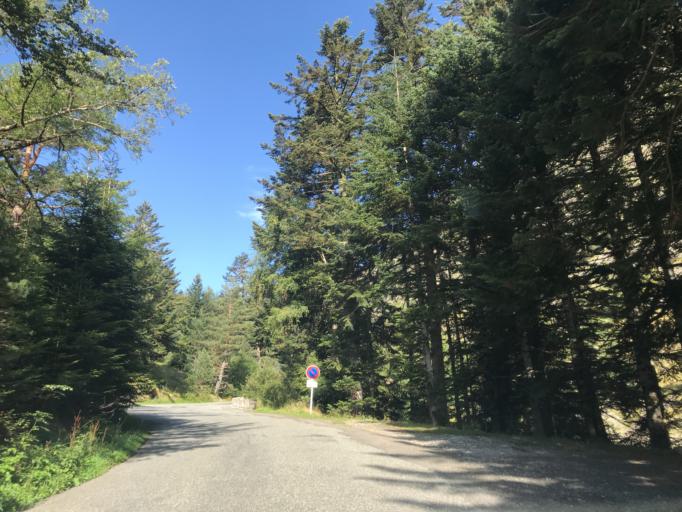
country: FR
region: Midi-Pyrenees
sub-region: Departement des Hautes-Pyrenees
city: Saint-Lary-Soulan
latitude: 42.8176
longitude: 0.1956
